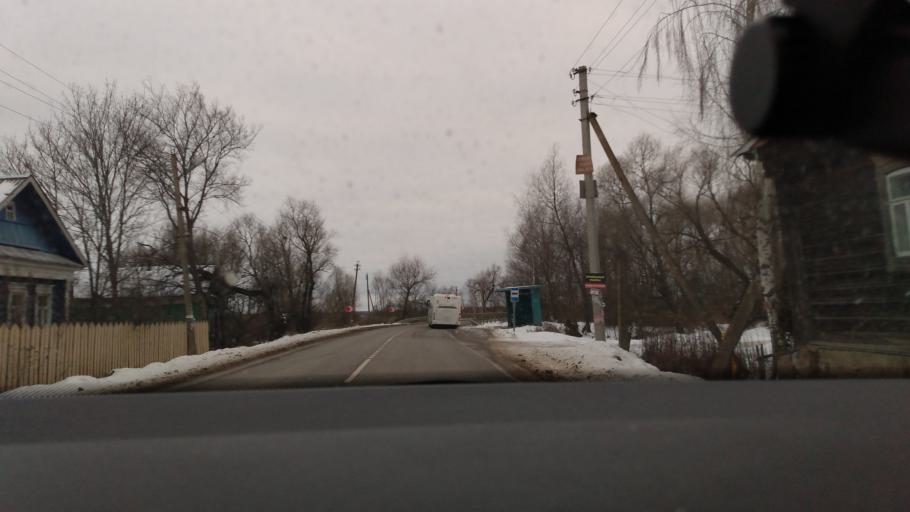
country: RU
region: Moskovskaya
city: Krasnaya Poyma
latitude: 55.1347
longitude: 39.1832
